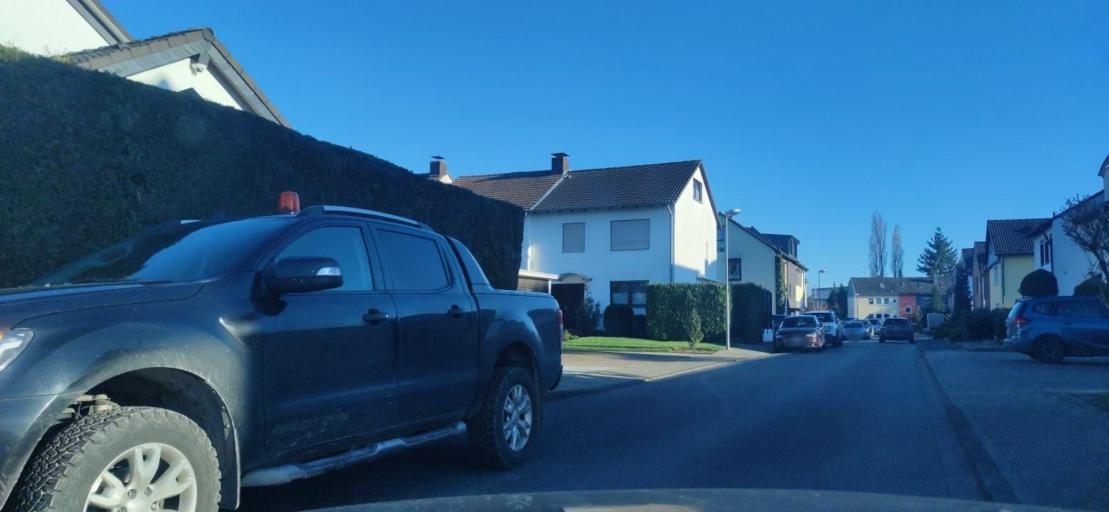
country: DE
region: North Rhine-Westphalia
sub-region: Regierungsbezirk Dusseldorf
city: Ratingen
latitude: 51.3098
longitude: 6.8283
